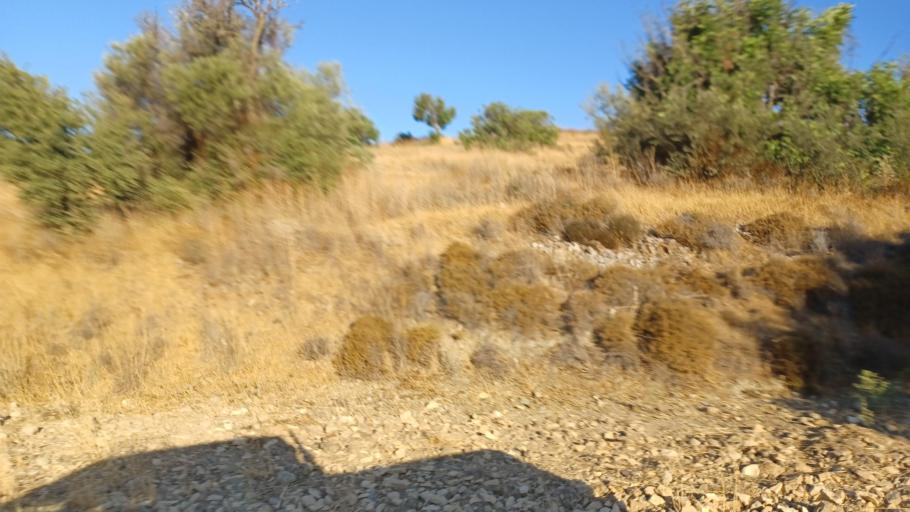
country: CY
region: Larnaka
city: Troulloi
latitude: 35.0275
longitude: 33.6506
